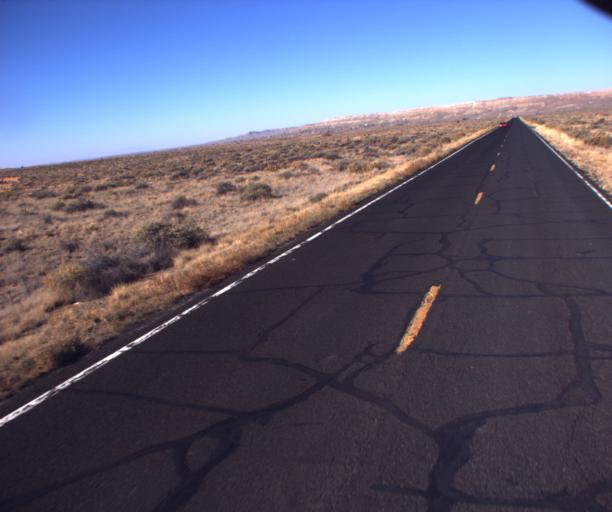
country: US
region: Arizona
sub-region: Navajo County
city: First Mesa
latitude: 35.8397
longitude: -110.3106
